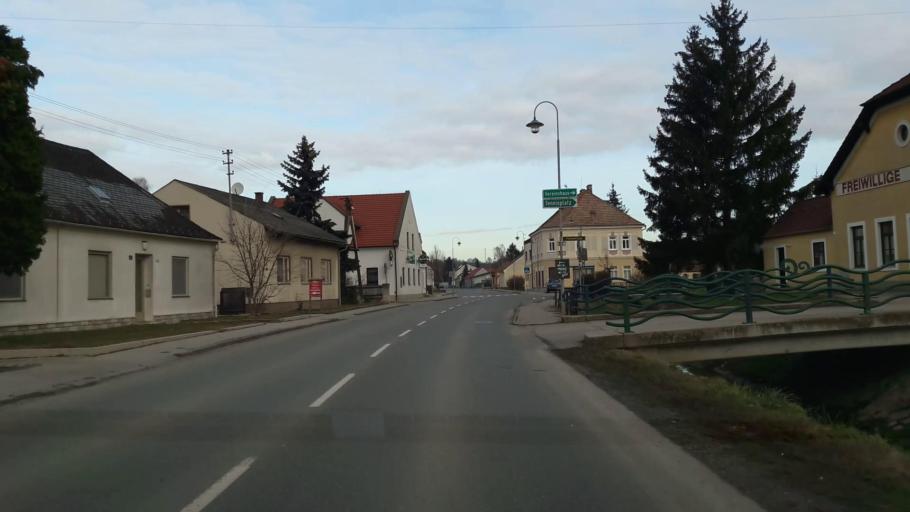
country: AT
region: Lower Austria
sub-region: Politischer Bezirk Mistelbach
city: Asparn an der Zaya
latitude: 48.6270
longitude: 16.5182
